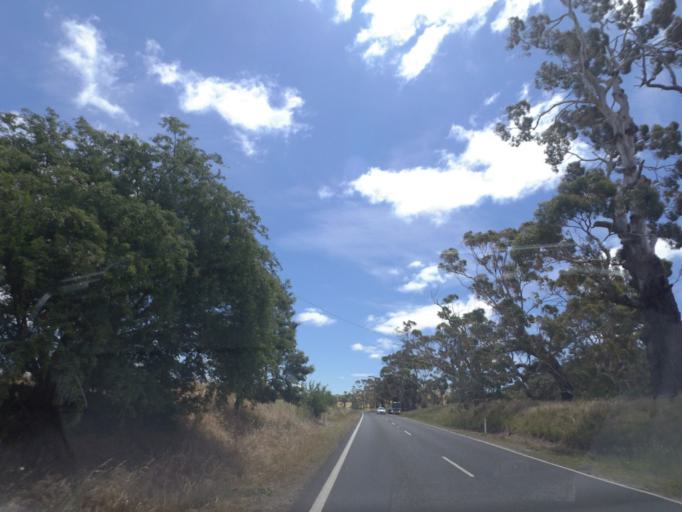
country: AU
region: Victoria
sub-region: Mount Alexander
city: Castlemaine
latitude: -37.2748
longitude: 144.1474
